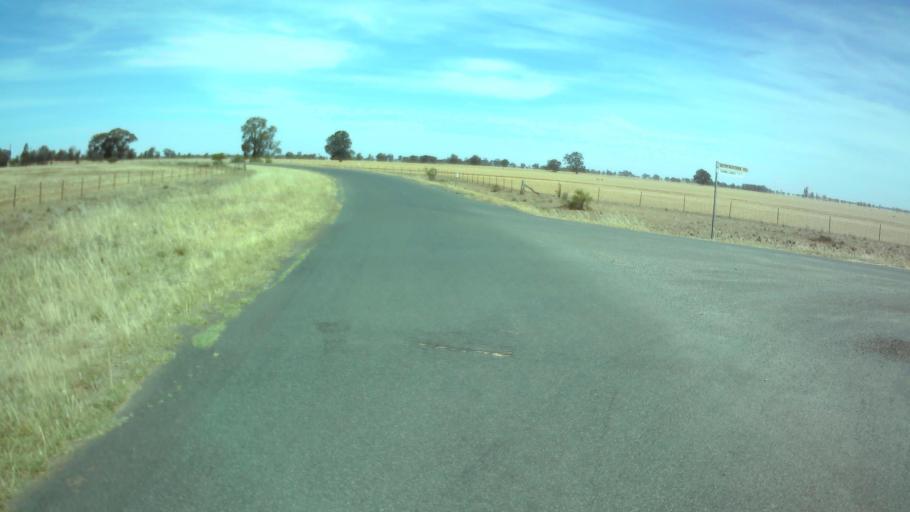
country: AU
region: New South Wales
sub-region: Weddin
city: Grenfell
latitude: -33.9391
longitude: 147.7625
